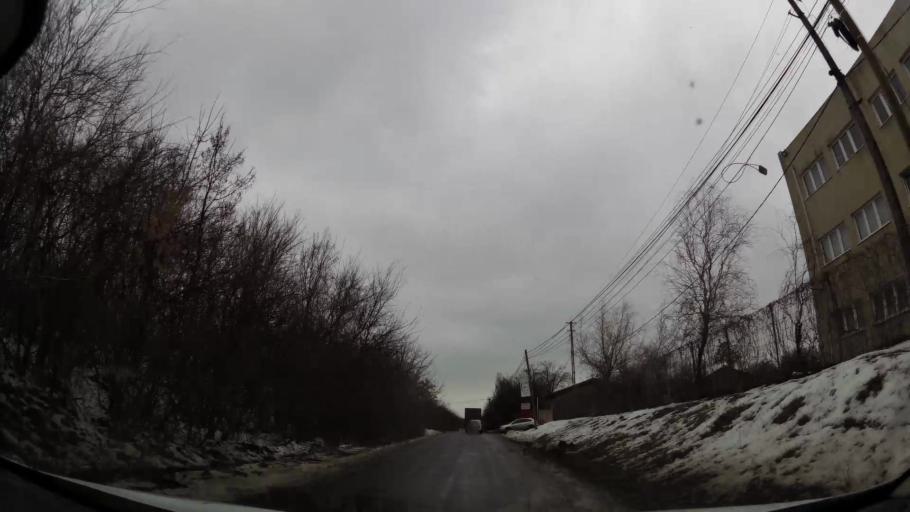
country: RO
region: Ilfov
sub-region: Comuna Chitila
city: Chitila
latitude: 44.4977
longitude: 26.0065
